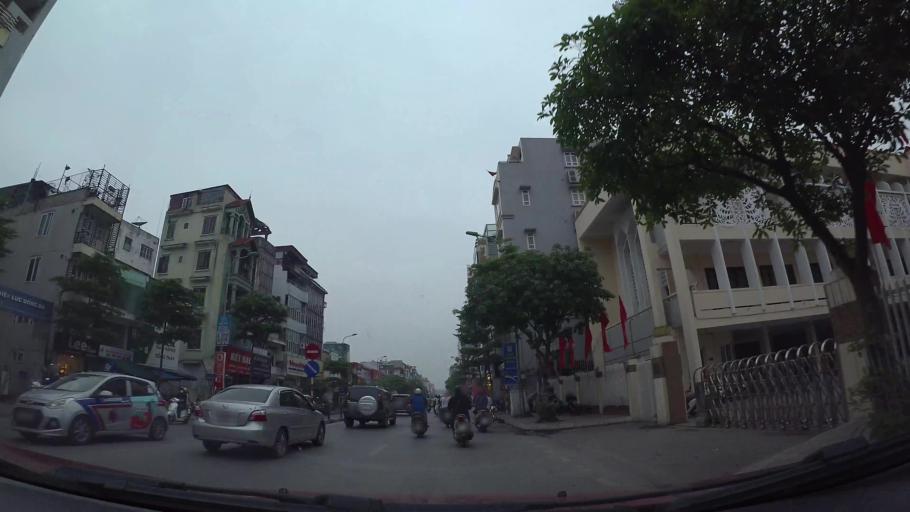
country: VN
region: Ha Noi
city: Dong Da
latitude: 21.0201
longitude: 105.8307
